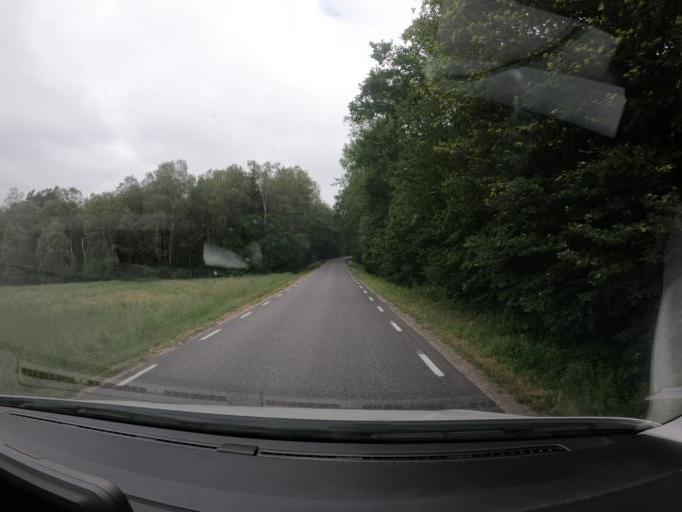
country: SE
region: Skane
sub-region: Hoors Kommun
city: Hoeoer
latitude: 56.0089
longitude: 13.4907
